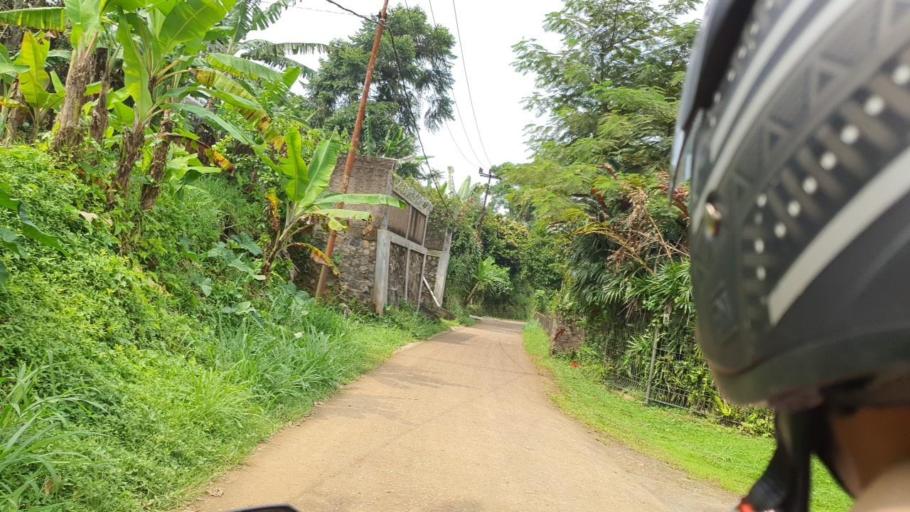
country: ID
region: West Java
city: Caringin
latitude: -6.6529
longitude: 106.8848
